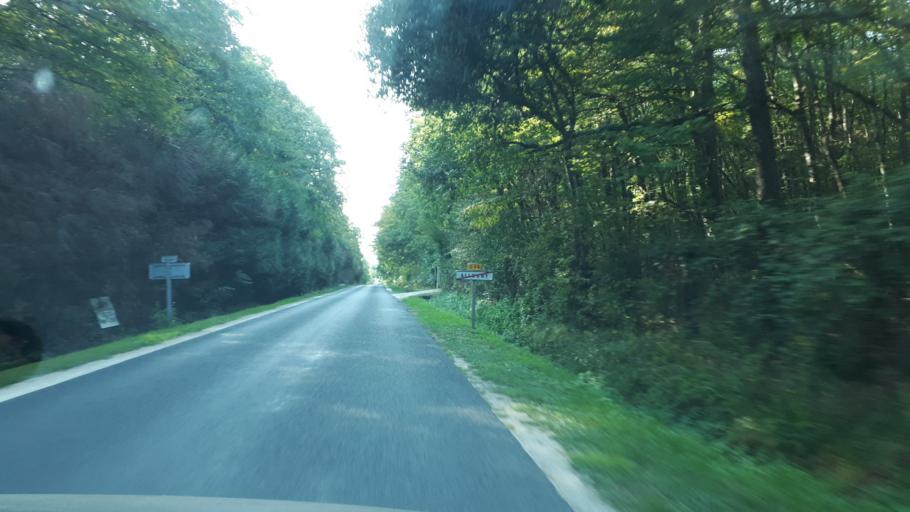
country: FR
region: Centre
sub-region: Departement du Cher
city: Saint-Eloy-de-Gy
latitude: 47.2260
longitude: 2.3089
